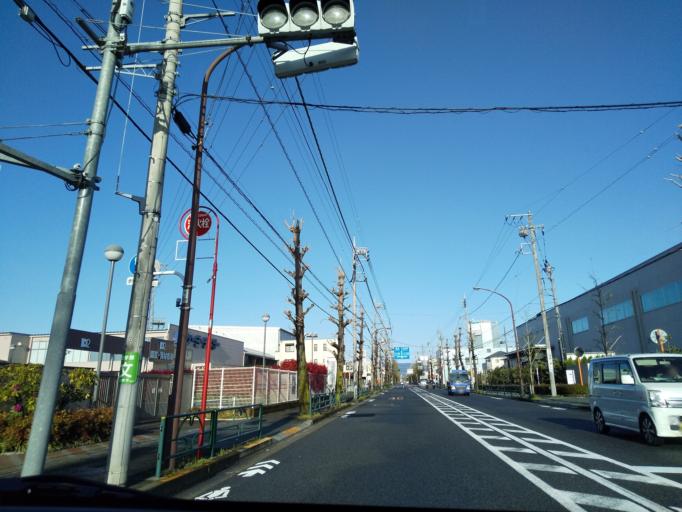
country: JP
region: Tokyo
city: Hino
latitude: 35.6590
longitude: 139.3701
